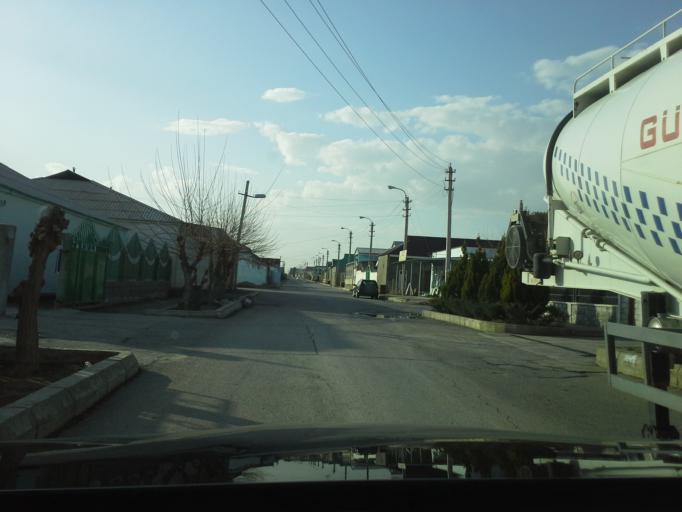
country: TM
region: Ahal
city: Abadan
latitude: 38.0206
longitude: 58.2289
